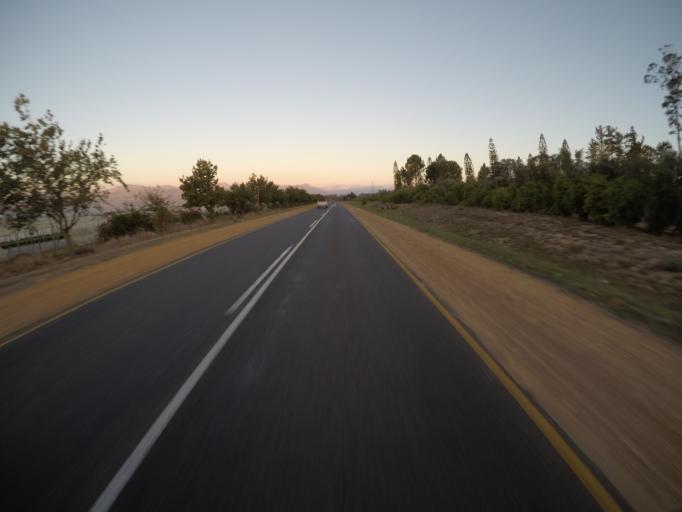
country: ZA
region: Western Cape
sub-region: Cape Winelands District Municipality
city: Paarl
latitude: -33.8039
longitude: 18.8931
